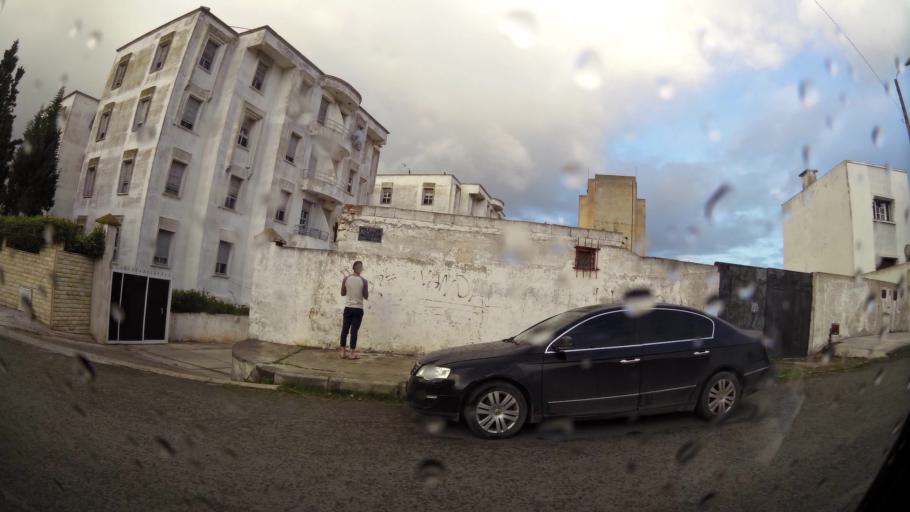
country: MA
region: Doukkala-Abda
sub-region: El-Jadida
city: El Jadida
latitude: 33.2419
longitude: -8.5005
